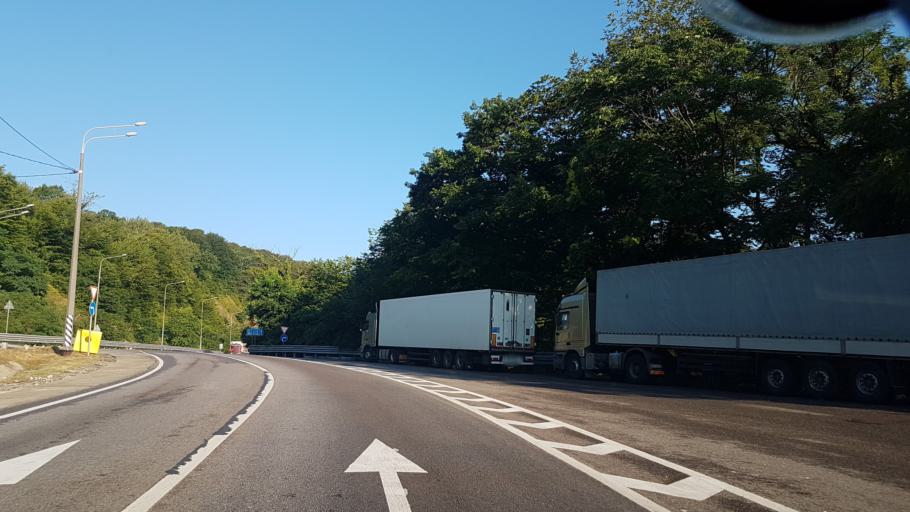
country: RU
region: Krasnodarskiy
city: Dagomys
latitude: 43.6461
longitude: 39.6946
